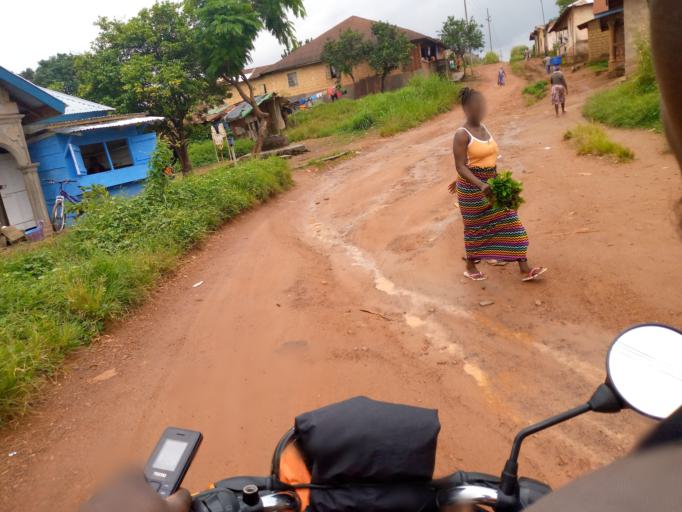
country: SL
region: Eastern Province
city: Kenema
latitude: 7.8724
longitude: -11.1834
